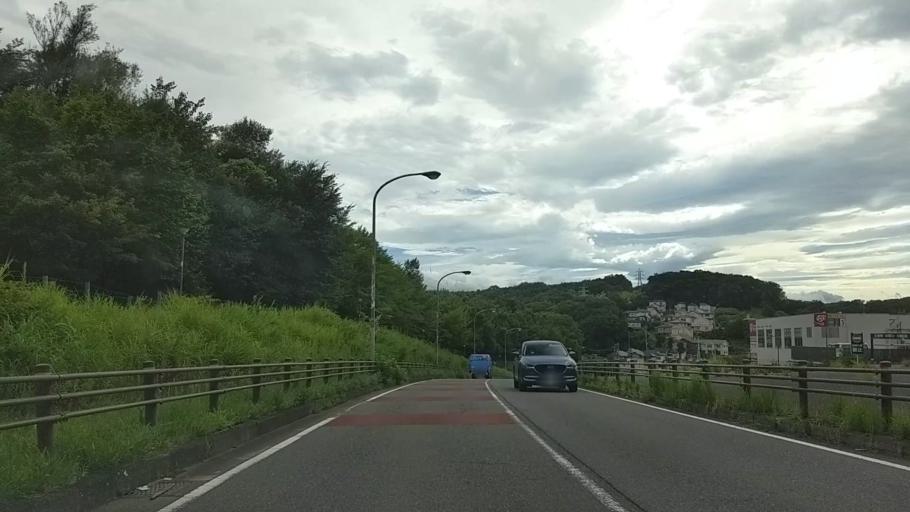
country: JP
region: Tokyo
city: Hachioji
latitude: 35.6302
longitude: 139.3162
